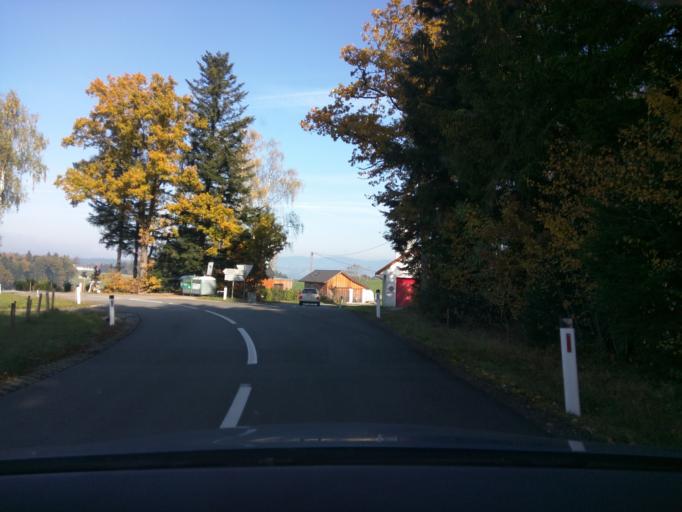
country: DE
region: Bavaria
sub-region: Lower Bavaria
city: Thyrnau
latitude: 48.5316
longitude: 13.5286
